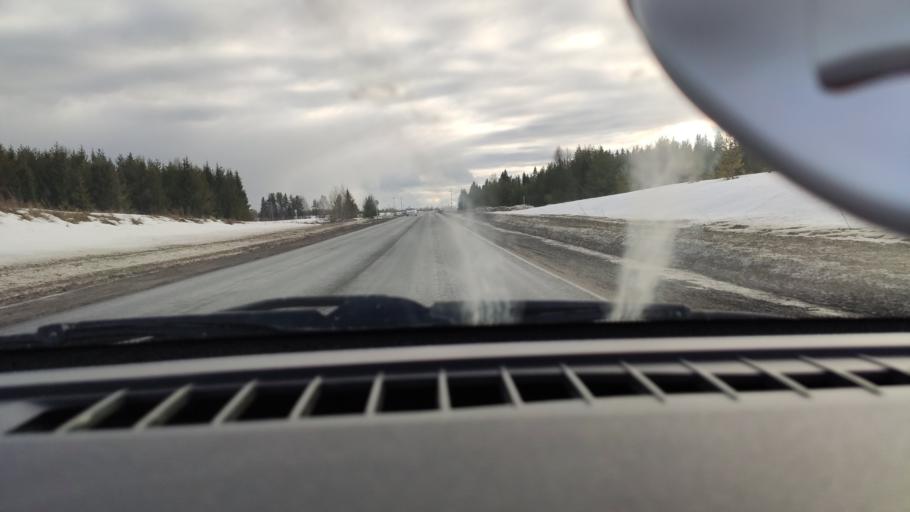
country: RU
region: Perm
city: Nytva
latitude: 57.9602
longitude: 55.3610
